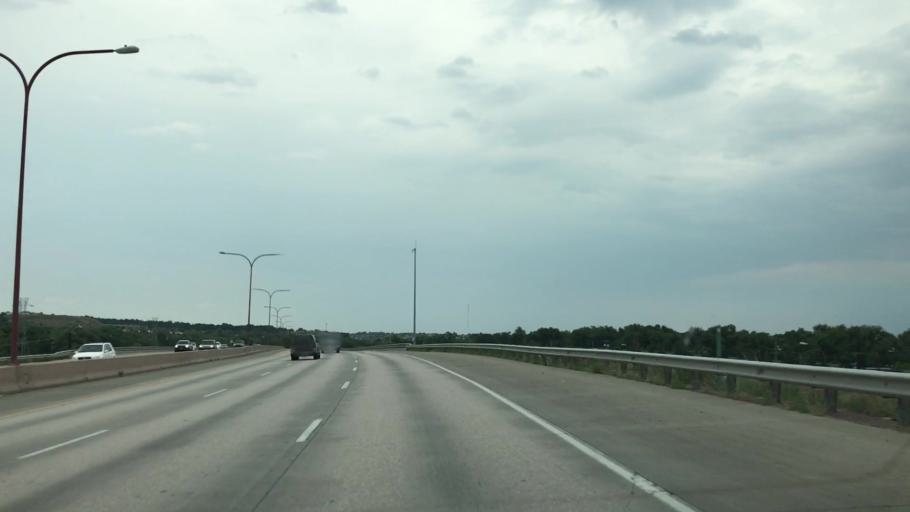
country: US
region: Colorado
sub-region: El Paso County
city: Colorado Springs
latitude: 38.8151
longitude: -104.8273
